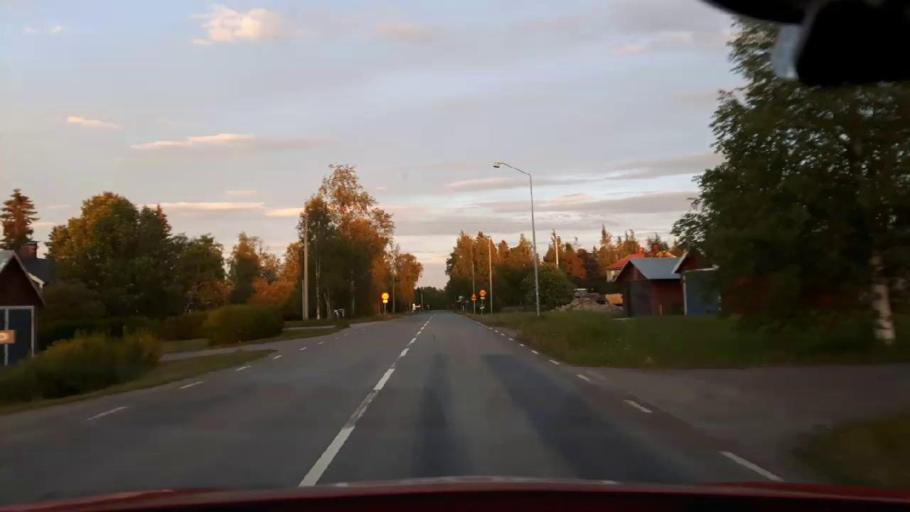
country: SE
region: Jaemtland
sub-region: OEstersunds Kommun
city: Brunflo
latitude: 63.1122
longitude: 14.7306
